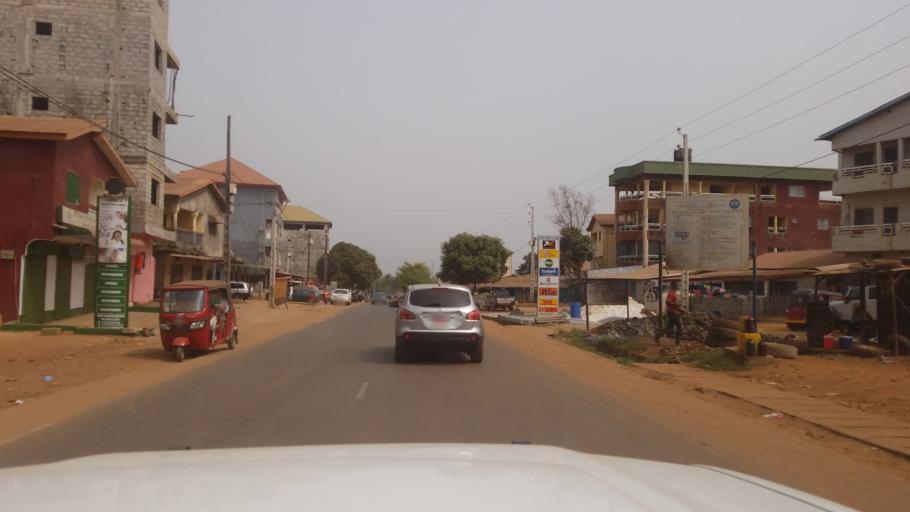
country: GN
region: Kindia
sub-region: Prefecture de Dubreka
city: Dubreka
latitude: 9.6647
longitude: -13.5928
